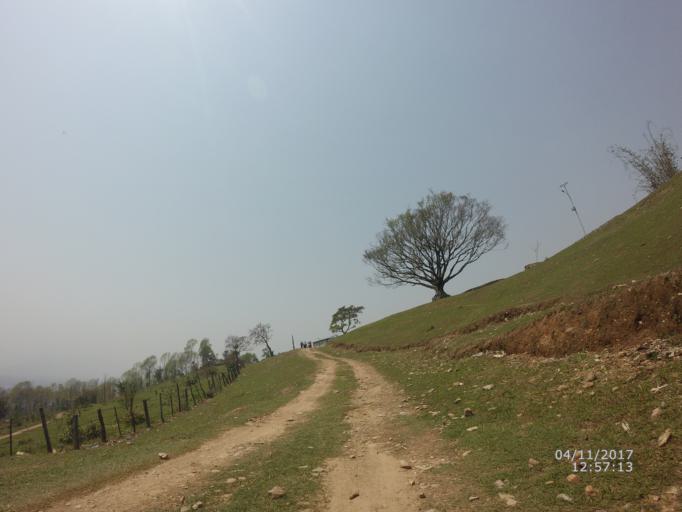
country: NP
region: Western Region
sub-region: Gandaki Zone
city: Pokhara
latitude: 28.2099
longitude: 84.0399
